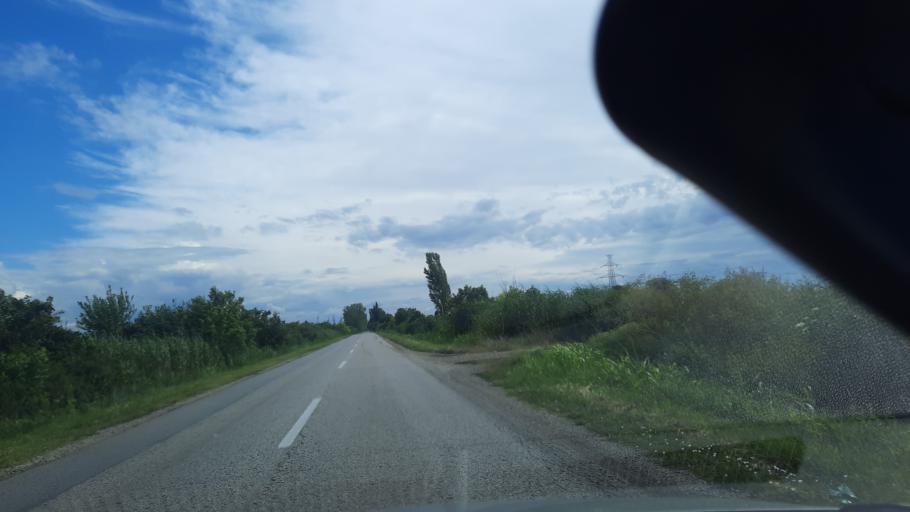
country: RS
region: Autonomna Pokrajina Vojvodina
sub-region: Sremski Okrug
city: Sremska Mitrovica
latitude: 45.0233
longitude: 19.6145
